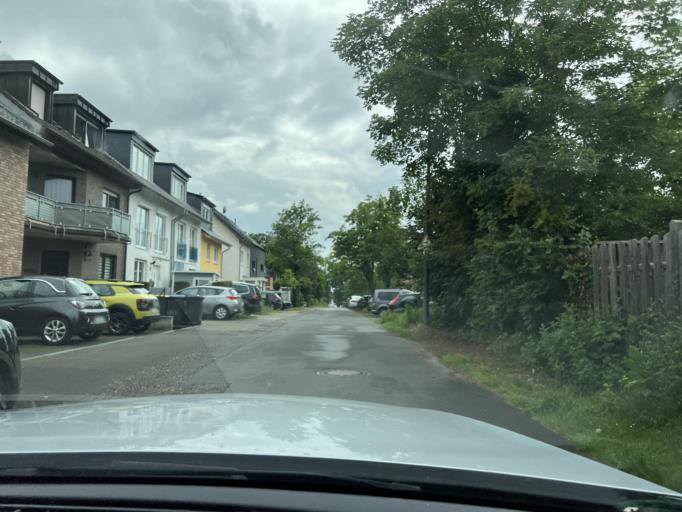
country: DE
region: North Rhine-Westphalia
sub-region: Regierungsbezirk Koln
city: Merheim
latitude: 50.9689
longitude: 7.0700
